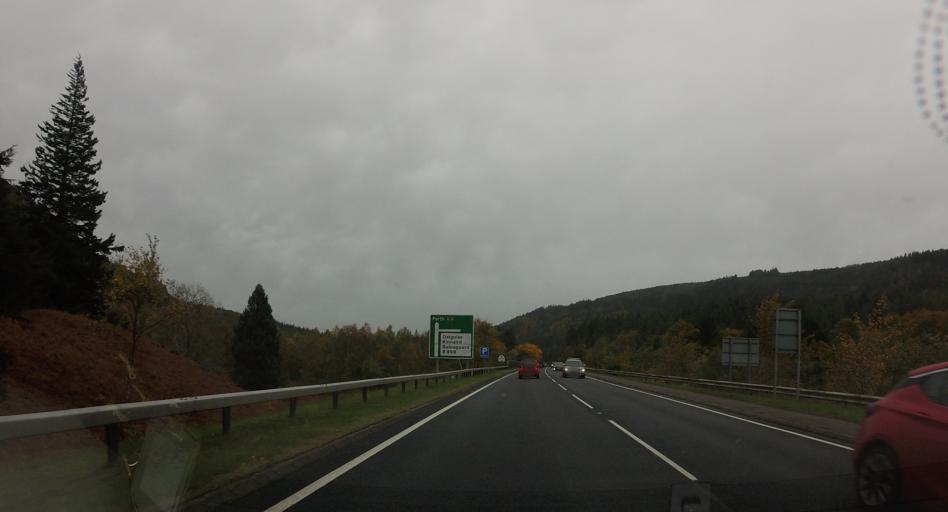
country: GB
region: Scotland
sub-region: Perth and Kinross
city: Bankfoot
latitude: 56.5776
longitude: -3.6211
